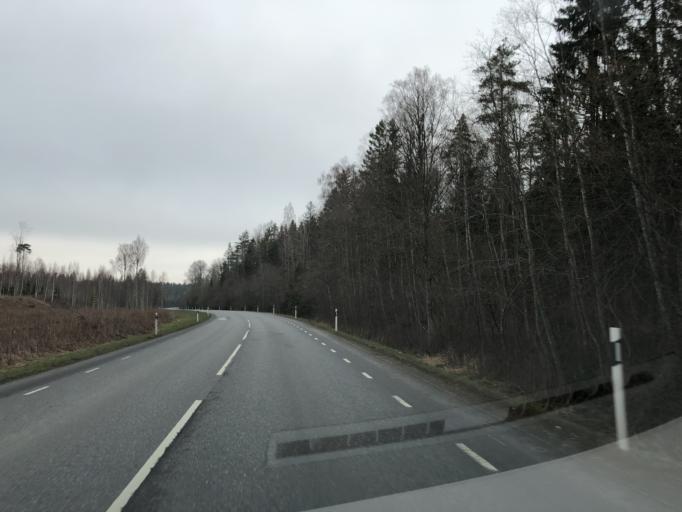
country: EE
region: Laeaene-Virumaa
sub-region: Vaeike-Maarja vald
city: Vaike-Maarja
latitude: 59.0875
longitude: 26.2365
